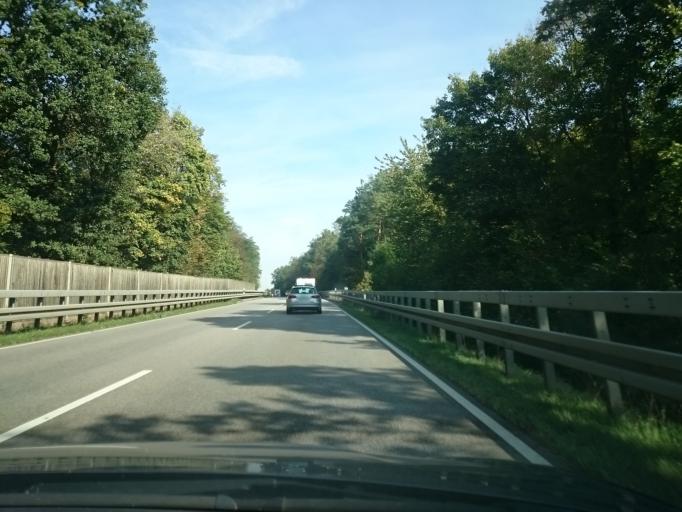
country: DE
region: Bavaria
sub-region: Upper Bavaria
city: Schrobenhausen
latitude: 48.5567
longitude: 11.2860
